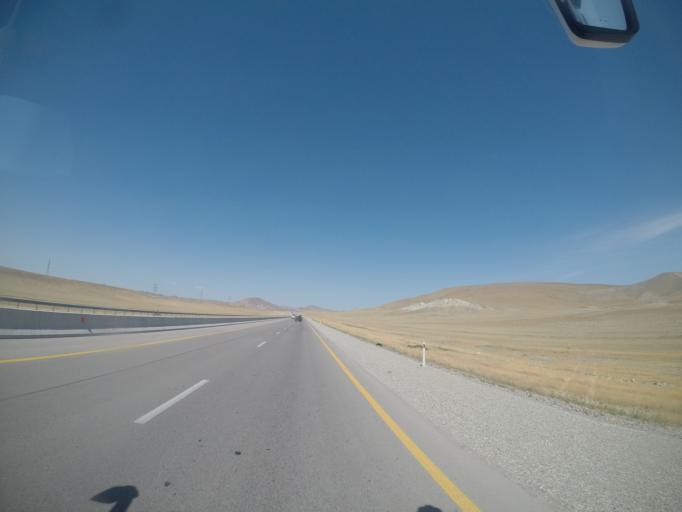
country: AZ
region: Sumqayit
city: Haci Zeynalabdin
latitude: 40.4949
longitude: 49.3480
